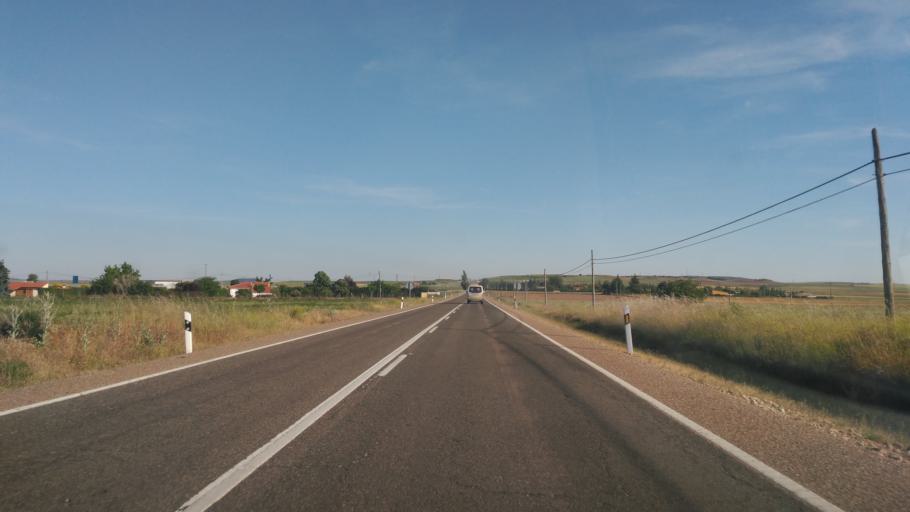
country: ES
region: Castille and Leon
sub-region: Provincia de Zamora
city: Morales del Vino
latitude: 41.4309
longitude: -5.7270
